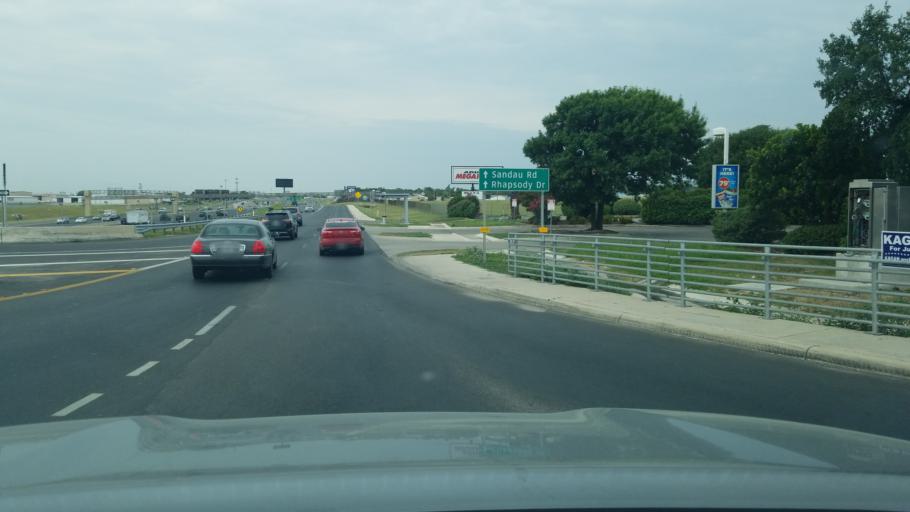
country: US
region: Texas
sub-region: Bexar County
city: Castle Hills
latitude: 29.5492
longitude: -98.4889
